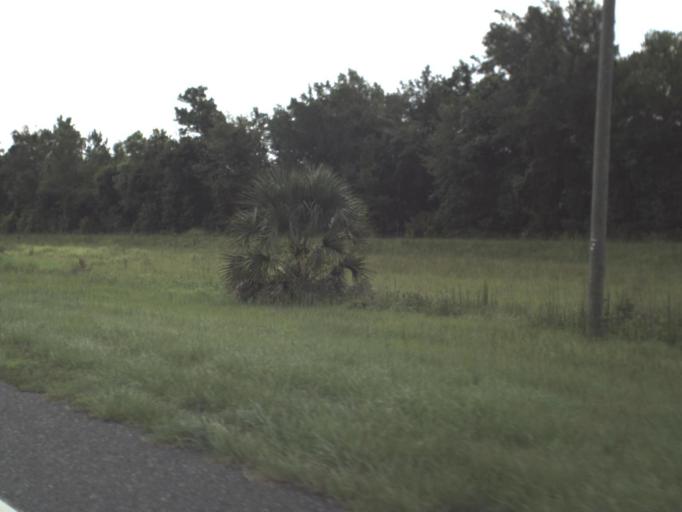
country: US
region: Florida
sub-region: Levy County
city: Inglis
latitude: 29.1962
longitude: -82.6883
